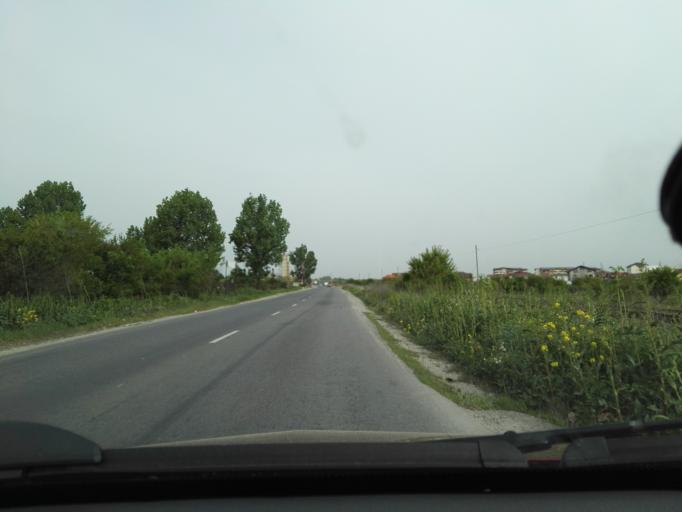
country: RO
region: Ilfov
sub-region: Comuna Magurele
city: Varteju
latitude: 44.3761
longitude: 26.0043
